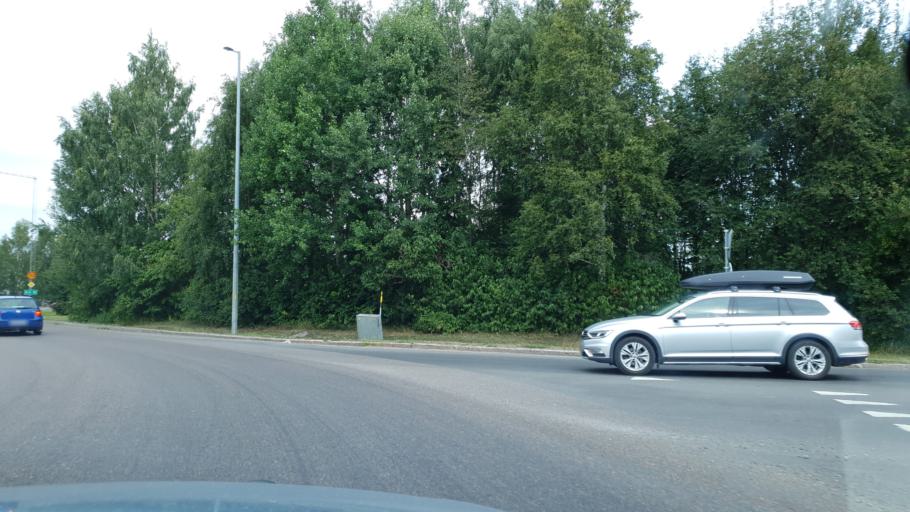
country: SE
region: Vaesterbotten
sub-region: Skelleftea Kommun
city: Skelleftea
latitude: 64.7434
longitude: 20.9617
